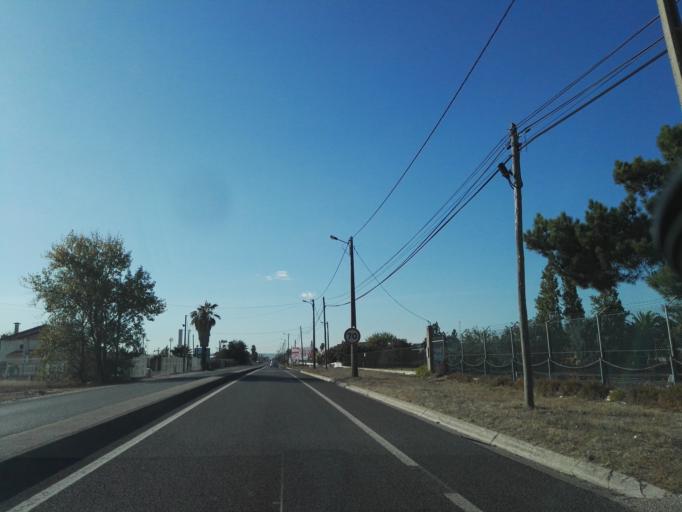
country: PT
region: Santarem
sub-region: Benavente
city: Samora Correia
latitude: 38.9147
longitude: -8.8603
